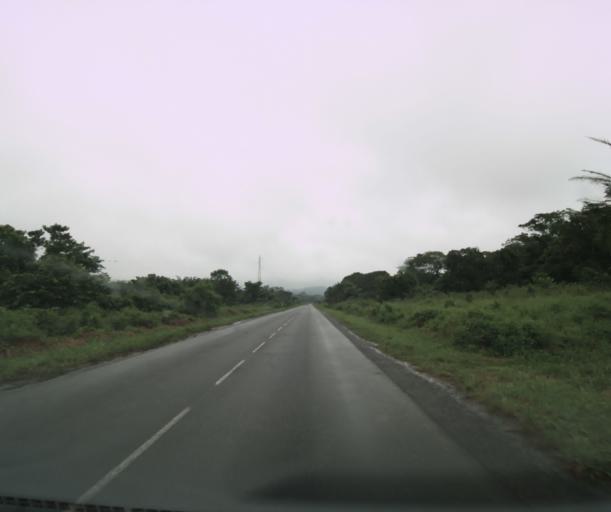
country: CM
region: Littoral
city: Edea
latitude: 3.6565
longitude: 10.1136
